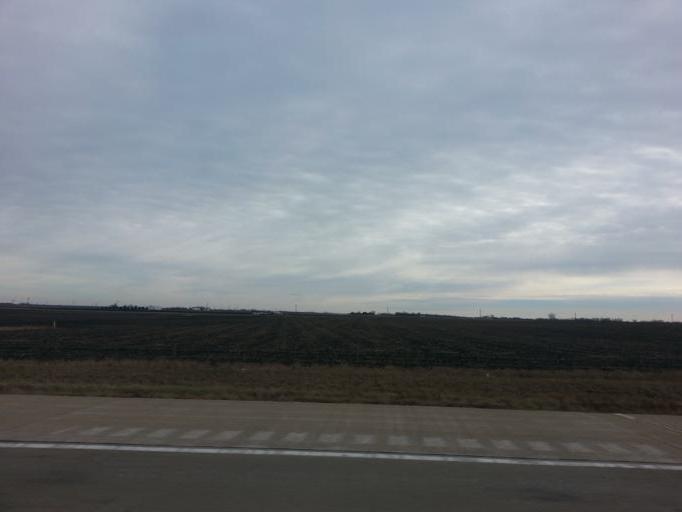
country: US
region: Illinois
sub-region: Woodford County
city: El Paso
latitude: 40.6892
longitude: -89.0289
